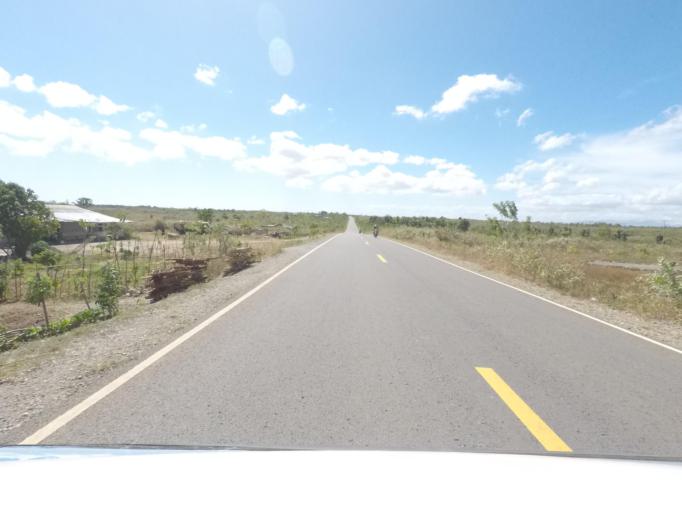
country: TL
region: Baucau
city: Baucau
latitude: -8.4865
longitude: 126.3779
